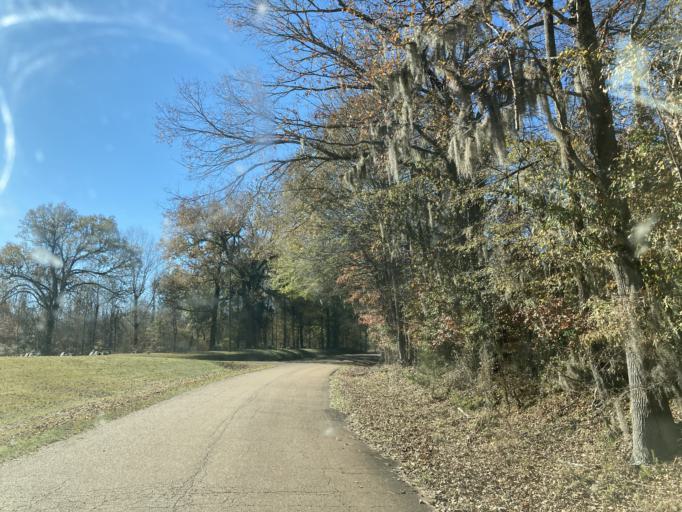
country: US
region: Mississippi
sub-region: Hinds County
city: Lynchburg
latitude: 32.5535
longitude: -90.5922
